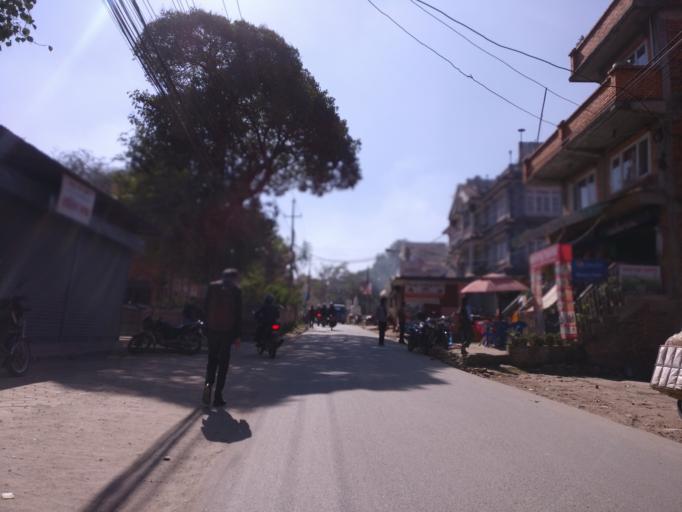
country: NP
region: Central Region
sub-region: Bagmati Zone
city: Patan
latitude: 27.6793
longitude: 85.3293
